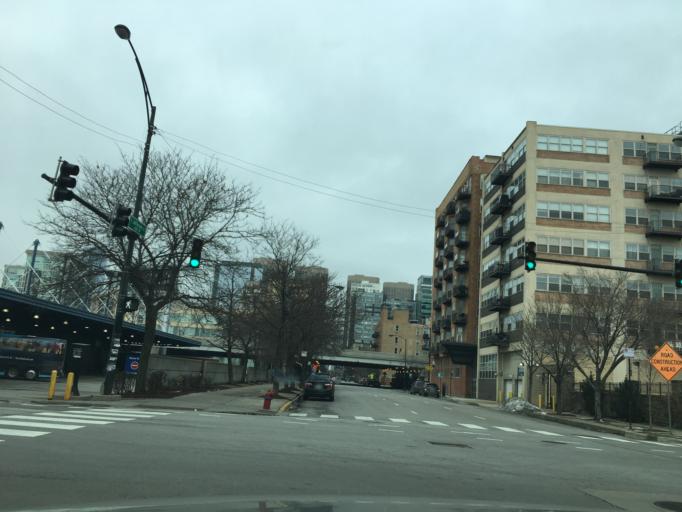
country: US
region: Illinois
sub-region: Cook County
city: Chicago
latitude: 41.8743
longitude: -87.6425
